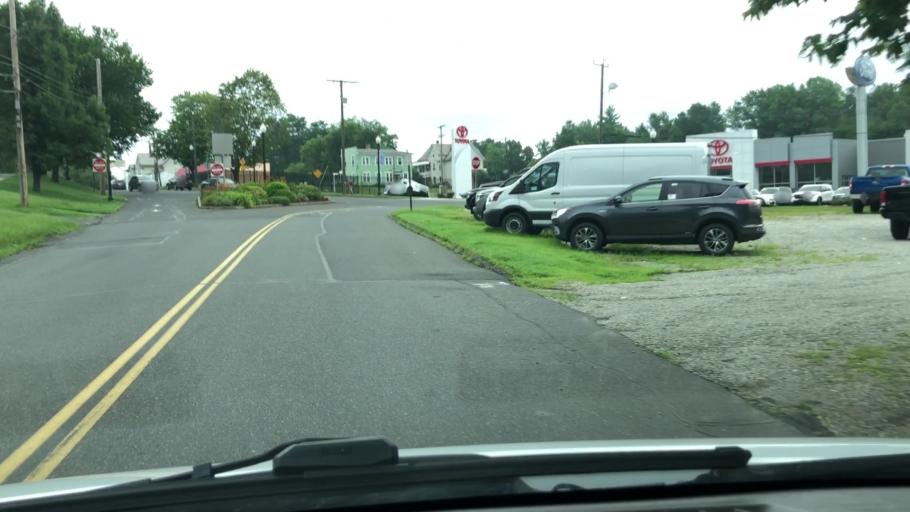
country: US
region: Massachusetts
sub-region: Franklin County
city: Greenfield
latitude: 42.5872
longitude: -72.6102
